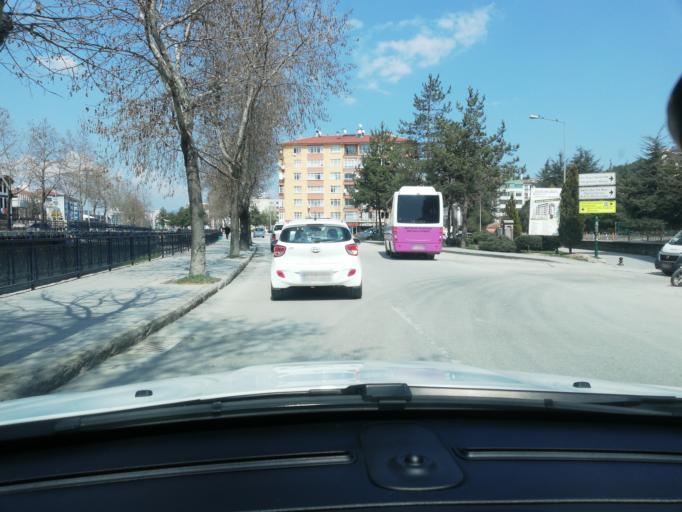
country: TR
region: Kastamonu
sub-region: Cide
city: Kastamonu
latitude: 41.3900
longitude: 33.7813
